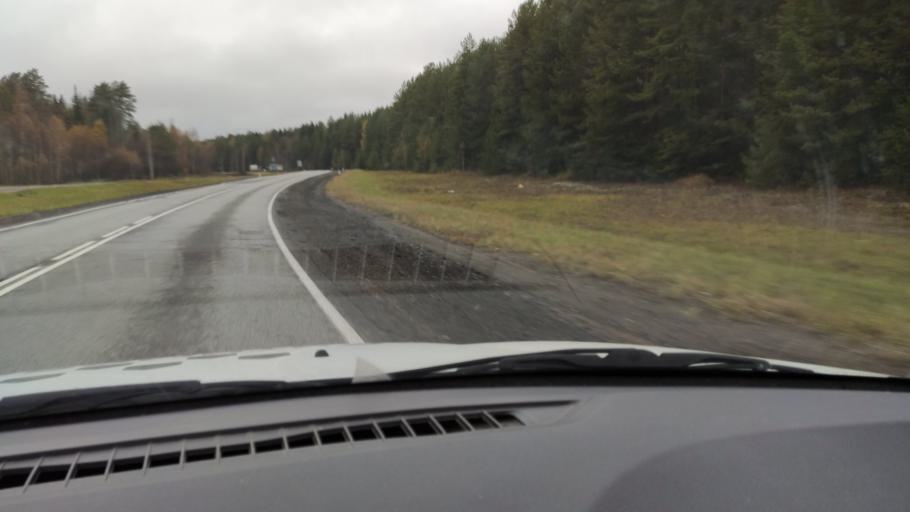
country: RU
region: Kirov
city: Belaya Kholunitsa
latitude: 58.8295
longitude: 50.6706
